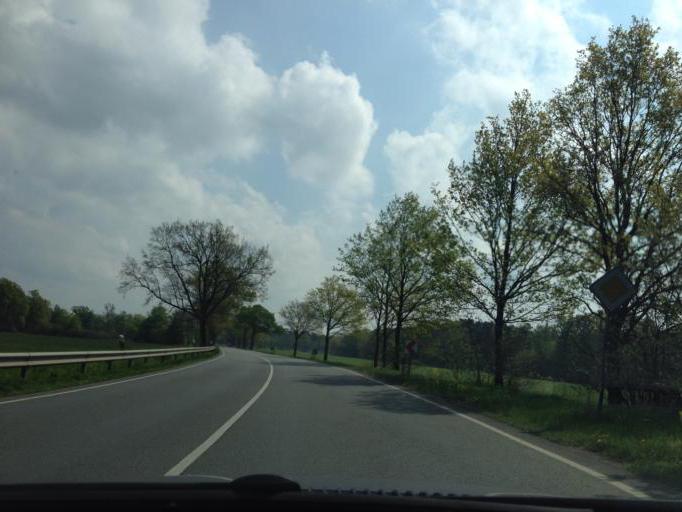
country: DE
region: Lower Saxony
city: Wathlingen
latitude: 52.5636
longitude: 10.1361
